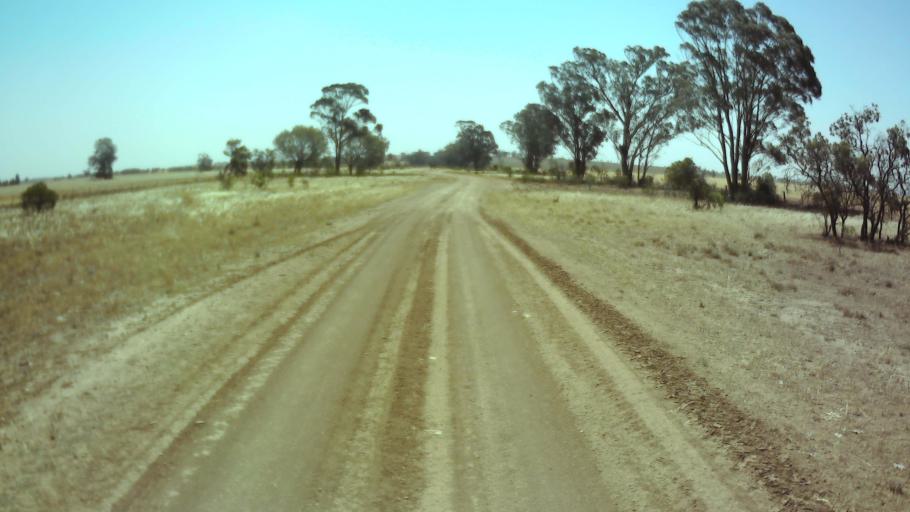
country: AU
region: New South Wales
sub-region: Weddin
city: Grenfell
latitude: -33.9169
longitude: 147.7750
